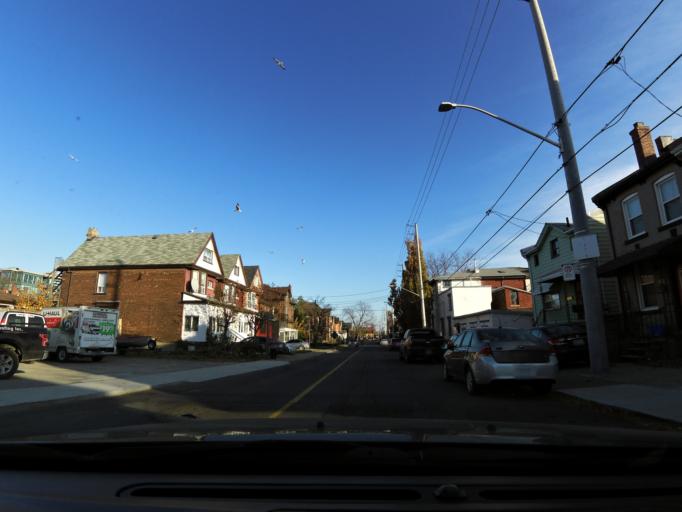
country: CA
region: Ontario
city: Hamilton
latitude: 43.2651
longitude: -79.8698
